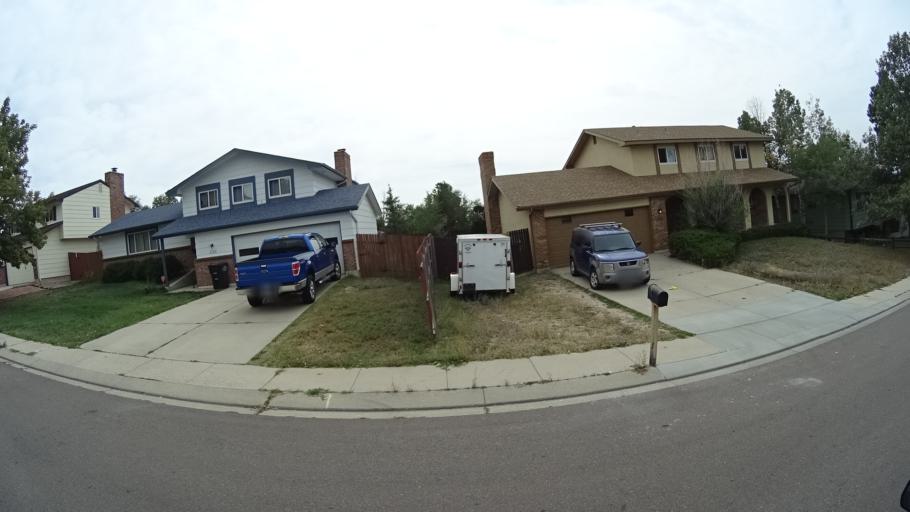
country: US
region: Colorado
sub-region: El Paso County
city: Cimarron Hills
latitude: 38.8897
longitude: -104.7318
